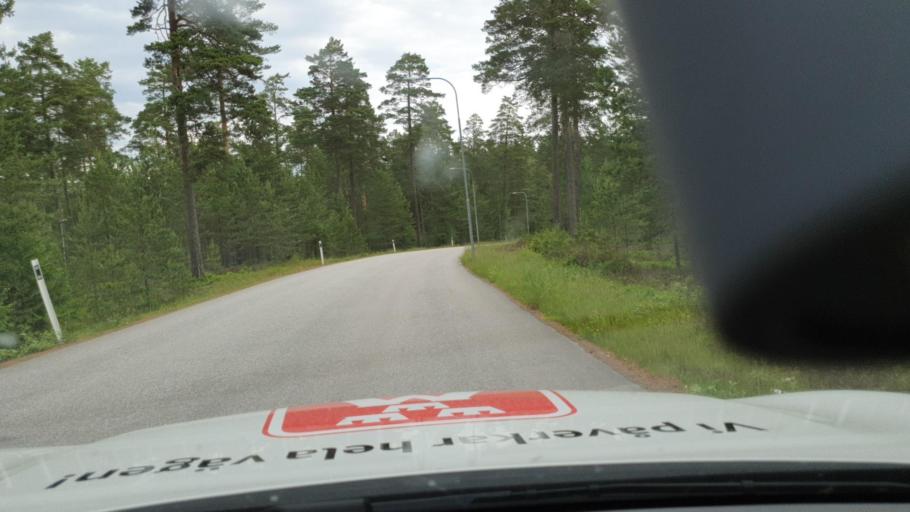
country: SE
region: Vaestra Goetaland
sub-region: Karlsborgs Kommun
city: Karlsborg
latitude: 58.5521
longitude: 14.4789
